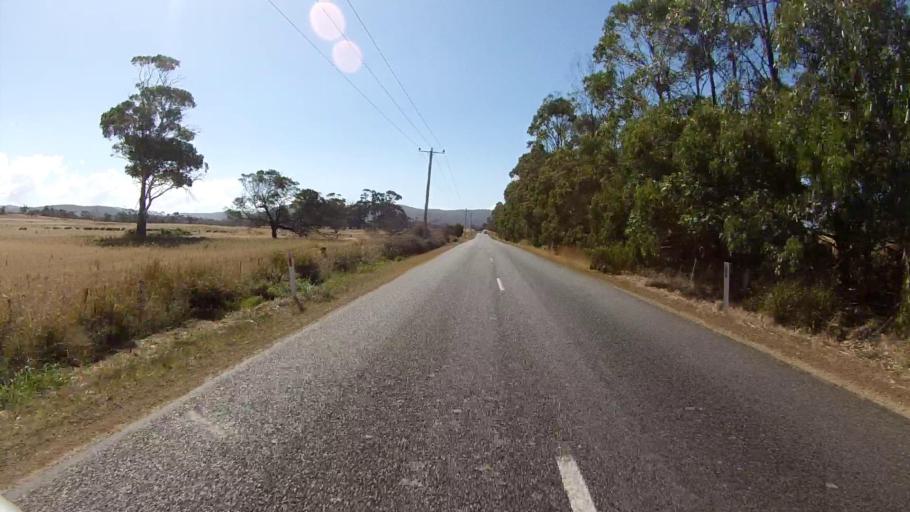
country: AU
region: Tasmania
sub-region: Sorell
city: Sorell
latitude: -42.2736
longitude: 148.0040
